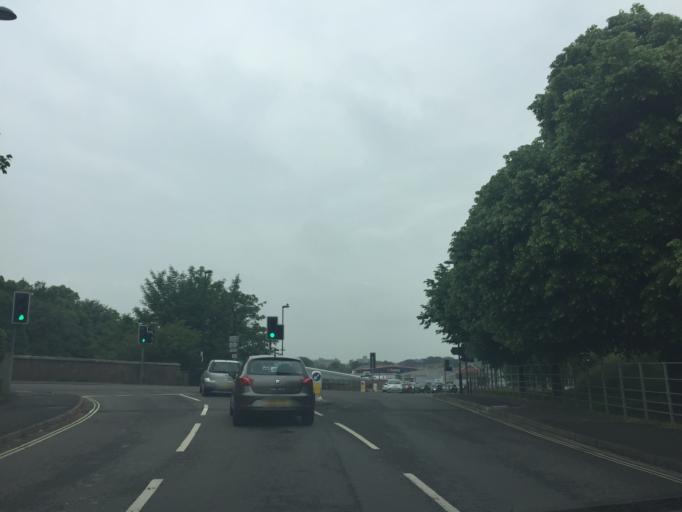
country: GB
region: England
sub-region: Dorset
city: Dorchester
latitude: 50.7077
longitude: -2.4410
